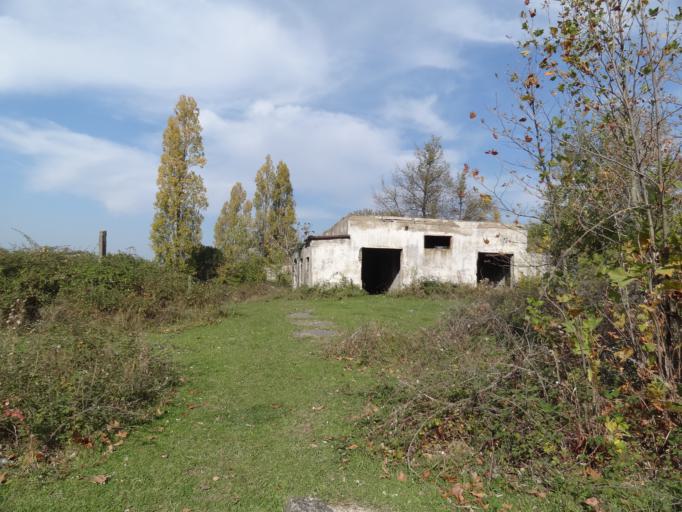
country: GE
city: Gantiadi
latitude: 43.3978
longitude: 40.0339
